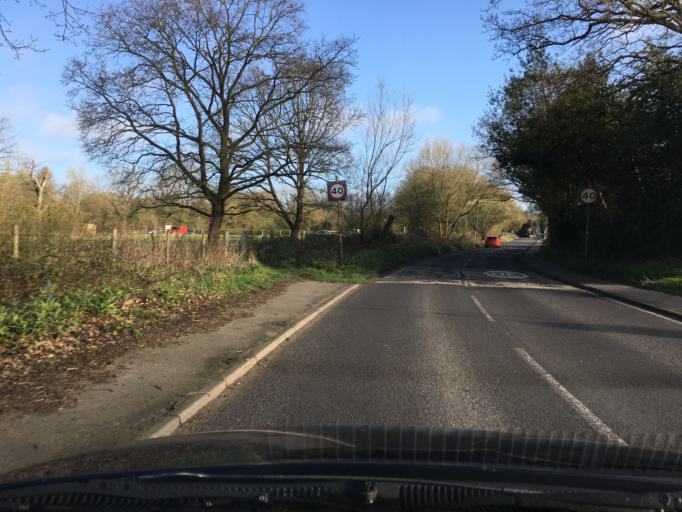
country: GB
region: England
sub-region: Bracknell Forest
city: Sandhurst
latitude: 51.3394
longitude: -0.8014
